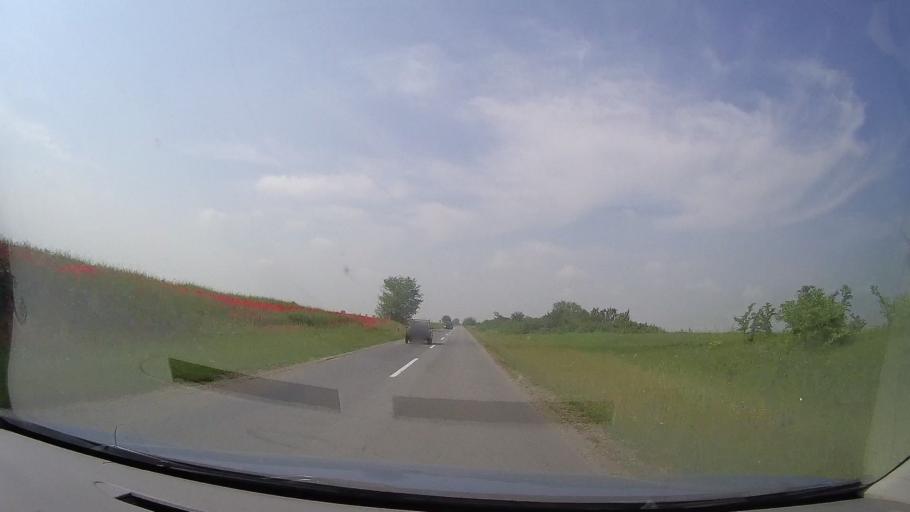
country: RS
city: Padina
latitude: 45.1526
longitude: 20.7458
